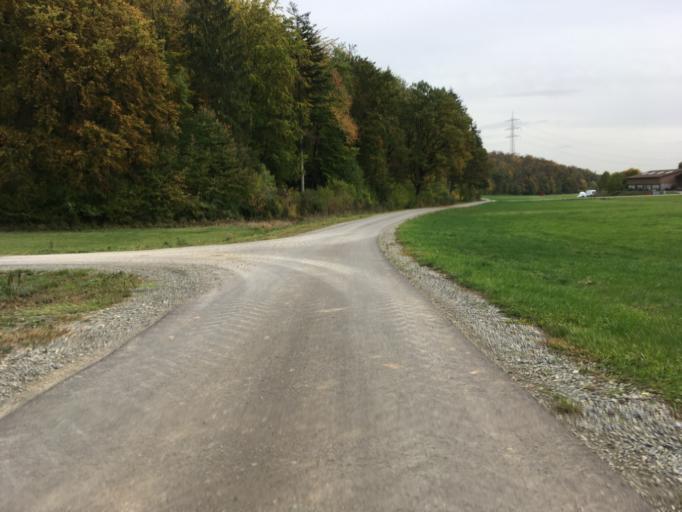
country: DE
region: Baden-Wuerttemberg
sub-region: Karlsruhe Region
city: Buchen
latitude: 49.4918
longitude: 9.3407
